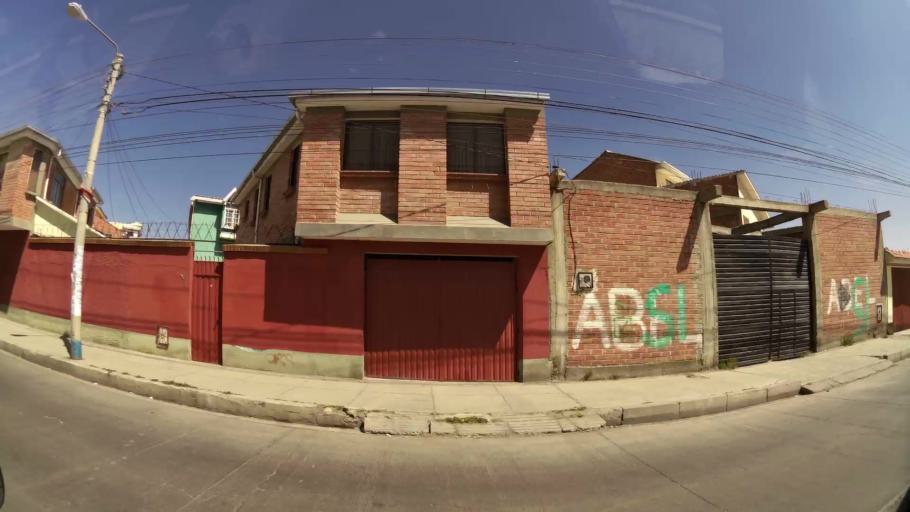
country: BO
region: La Paz
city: La Paz
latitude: -16.5260
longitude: -68.1468
